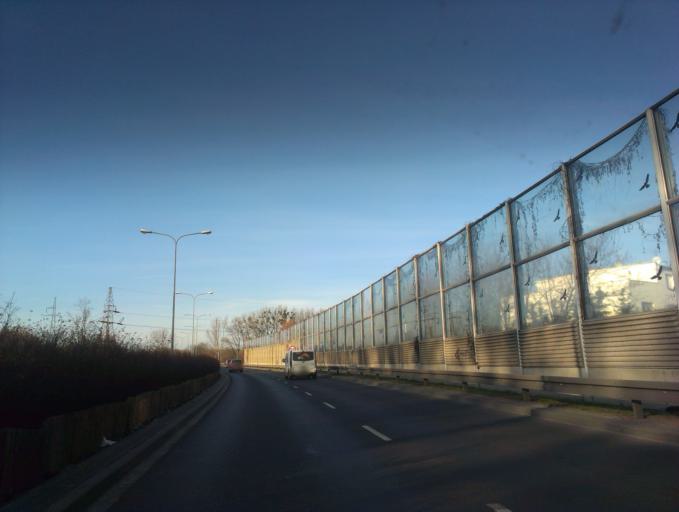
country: PL
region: Greater Poland Voivodeship
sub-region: Poznan
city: Poznan
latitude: 52.4392
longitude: 16.9516
